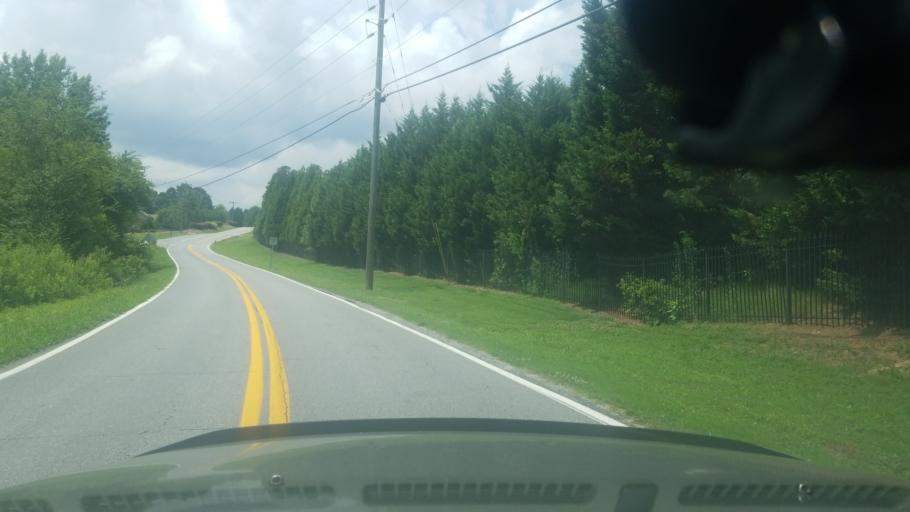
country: US
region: Georgia
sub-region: Fulton County
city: Johns Creek
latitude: 34.1042
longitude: -84.1903
